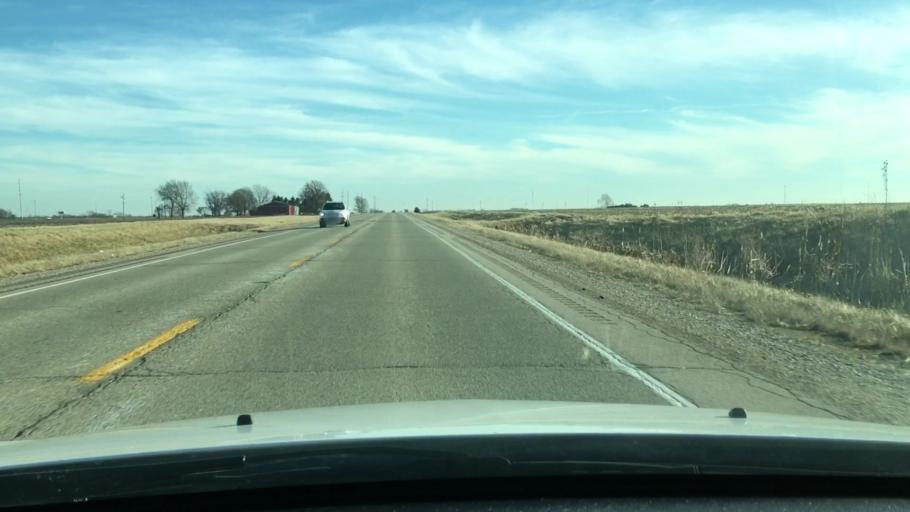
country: US
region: Illinois
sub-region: LaSalle County
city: Oglesby
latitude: 41.2865
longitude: -89.0923
